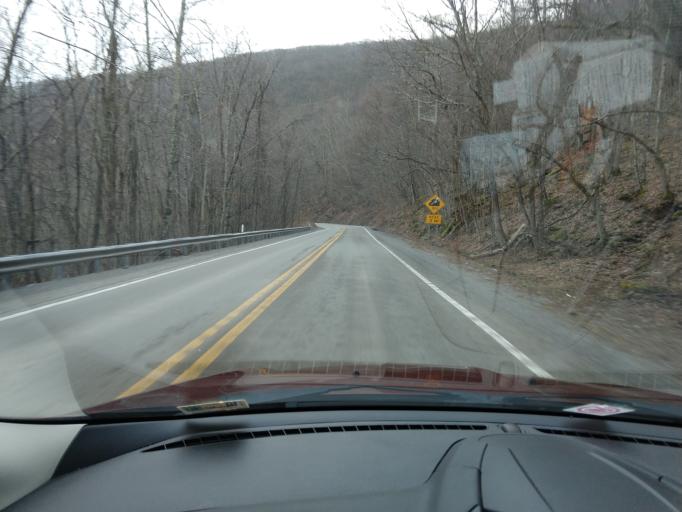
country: US
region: West Virginia
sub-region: Randolph County
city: Elkins
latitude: 38.6418
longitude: -79.9226
